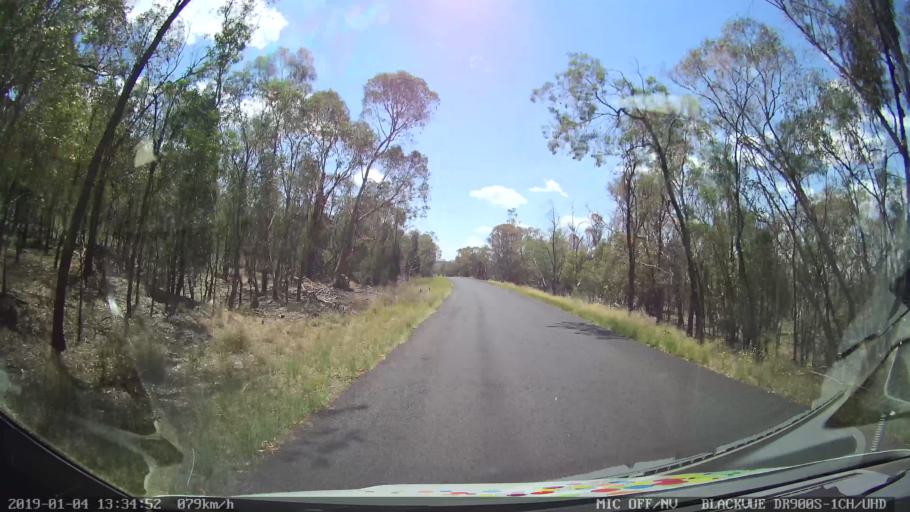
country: AU
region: New South Wales
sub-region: Dubbo Municipality
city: Dubbo
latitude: -32.5801
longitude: 148.5362
